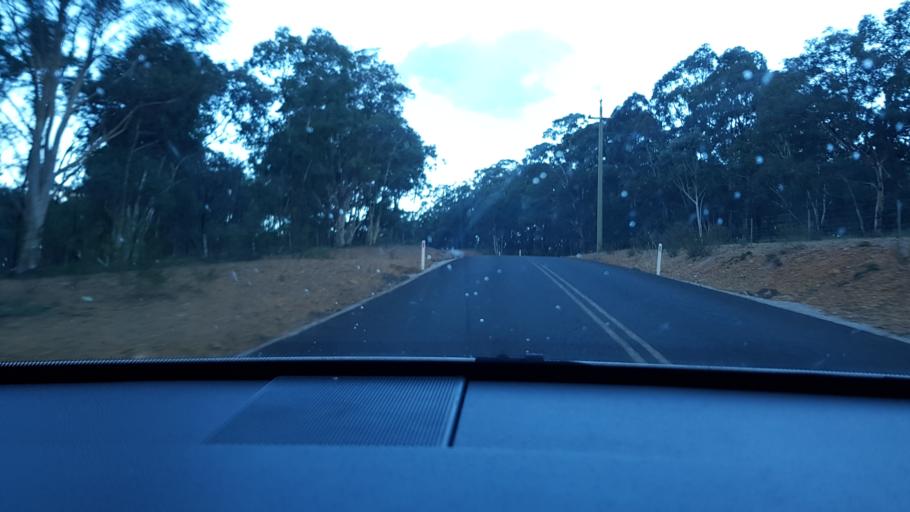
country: AU
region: New South Wales
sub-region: Lithgow
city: Portland
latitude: -33.2622
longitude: 150.1286
